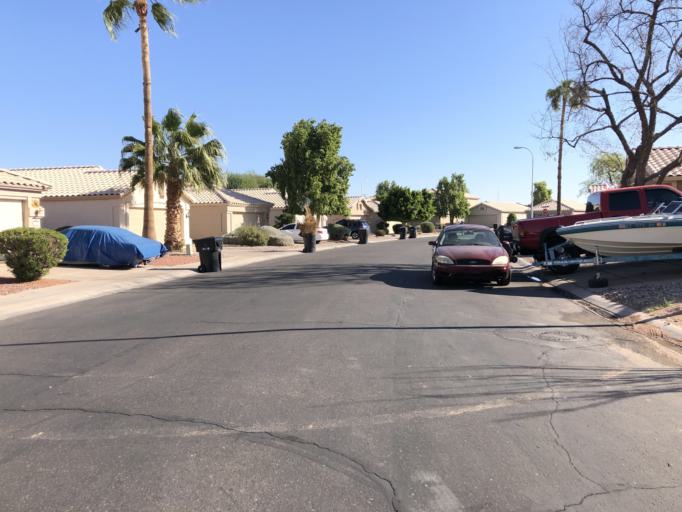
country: US
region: Arizona
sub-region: Maricopa County
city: Guadalupe
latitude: 33.3150
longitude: -111.9211
